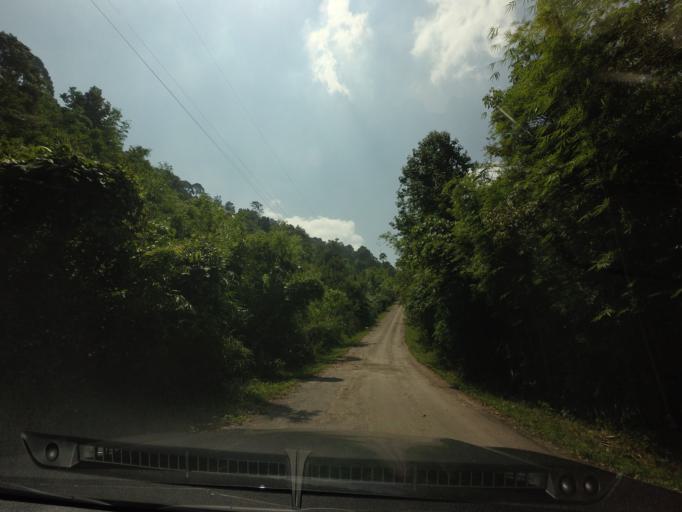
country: TH
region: Loei
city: Na Haeo
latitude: 17.5288
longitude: 100.9378
